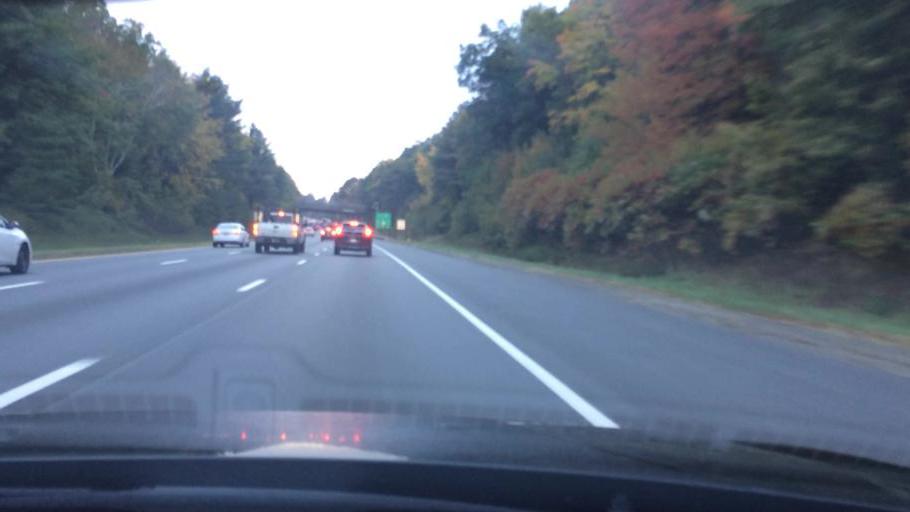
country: US
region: Massachusetts
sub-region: Essex County
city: Lawrence
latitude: 42.6733
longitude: -71.1780
